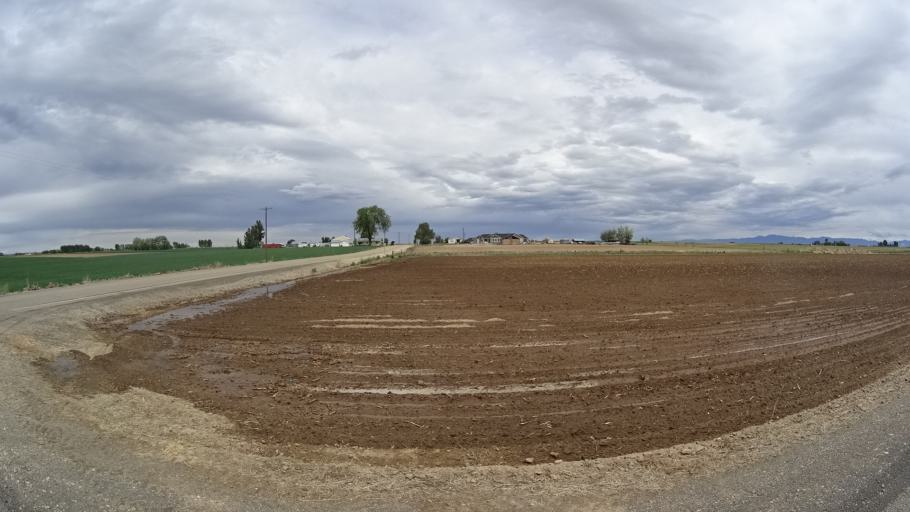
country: US
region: Idaho
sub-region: Canyon County
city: Nampa
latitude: 43.4591
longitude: -116.5135
